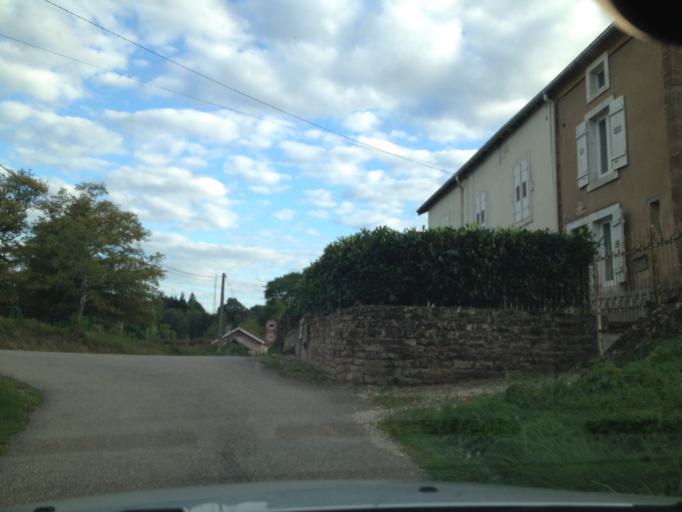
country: FR
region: Lorraine
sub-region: Departement des Vosges
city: Bains-les-Bains
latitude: 47.9790
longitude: 6.2016
